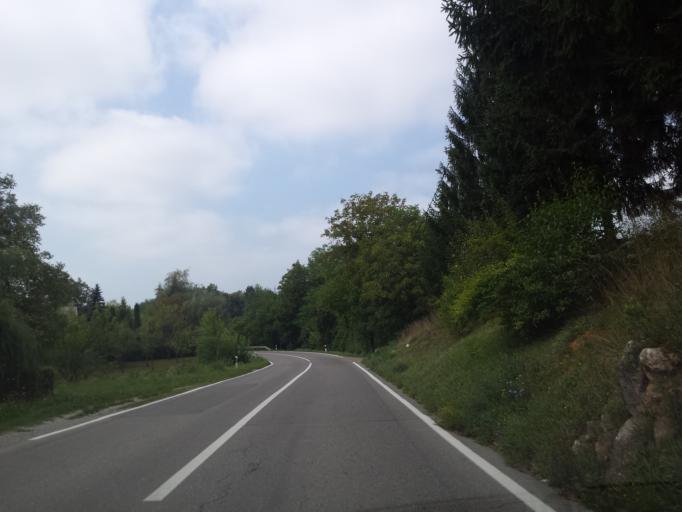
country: HR
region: Karlovacka
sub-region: Grad Karlovac
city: Karlovac
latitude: 45.3653
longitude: 15.4045
